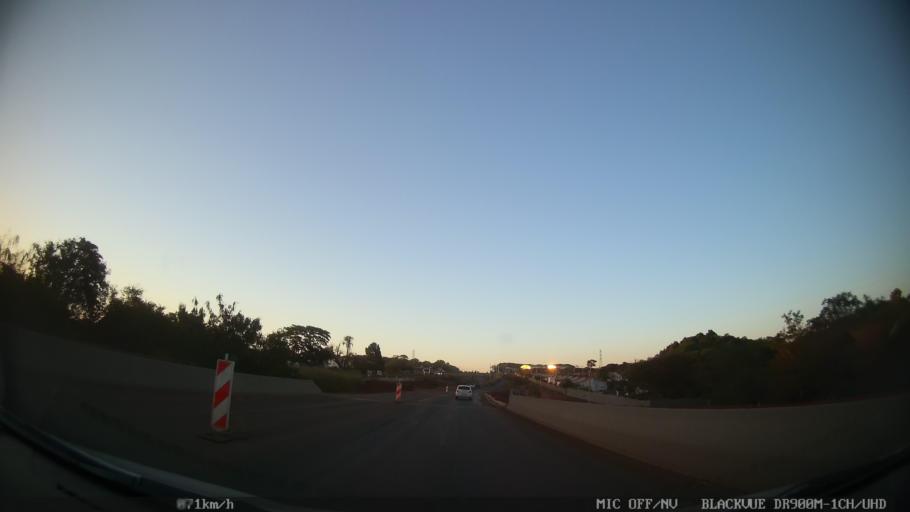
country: BR
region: Sao Paulo
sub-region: Sao Jose Do Rio Preto
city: Sao Jose do Rio Preto
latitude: -20.7757
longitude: -49.3521
